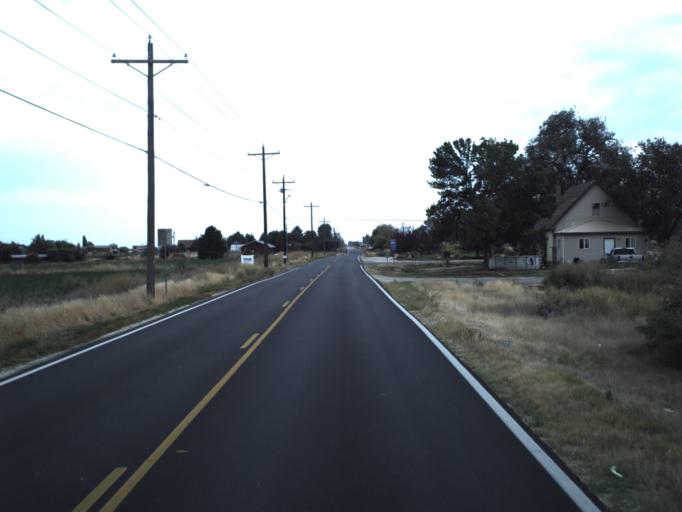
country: US
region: Utah
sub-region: Weber County
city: West Haven
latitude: 41.2336
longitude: -112.0928
